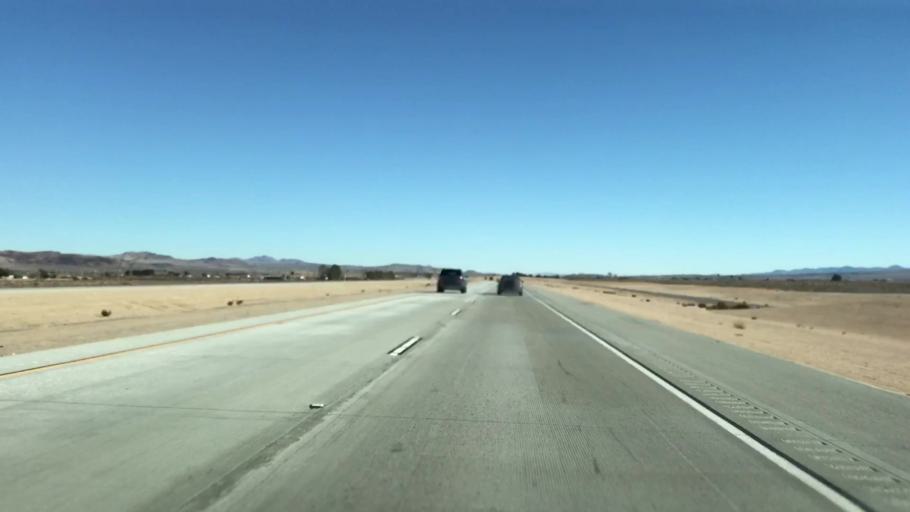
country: US
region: California
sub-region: San Bernardino County
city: Lenwood
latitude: 34.9135
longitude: -117.2080
